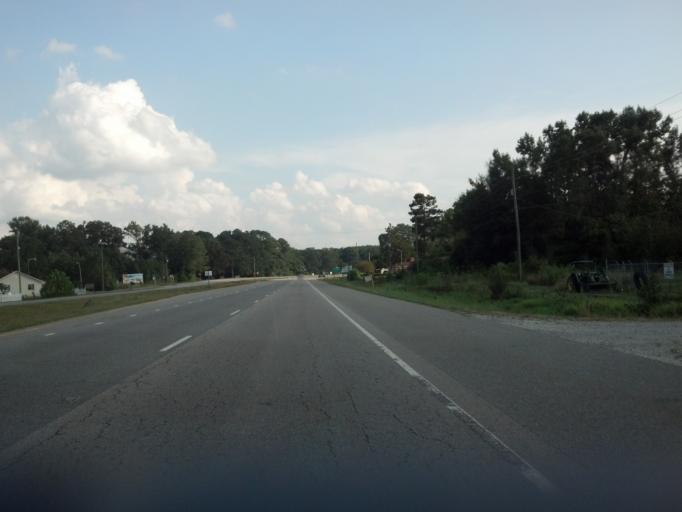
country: US
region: North Carolina
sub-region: Pitt County
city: Greenville
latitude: 35.6745
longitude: -77.3633
